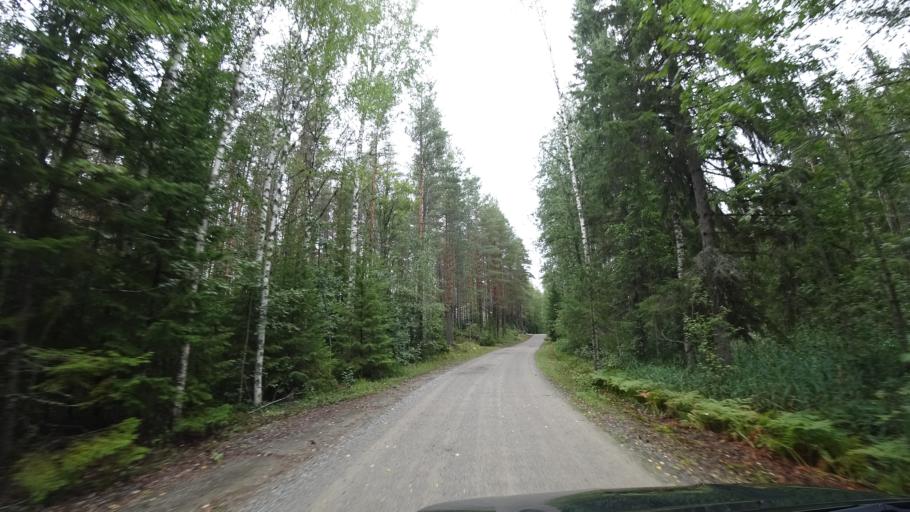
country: FI
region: Paijanne Tavastia
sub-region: Lahti
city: Auttoinen
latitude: 61.2204
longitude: 25.1412
